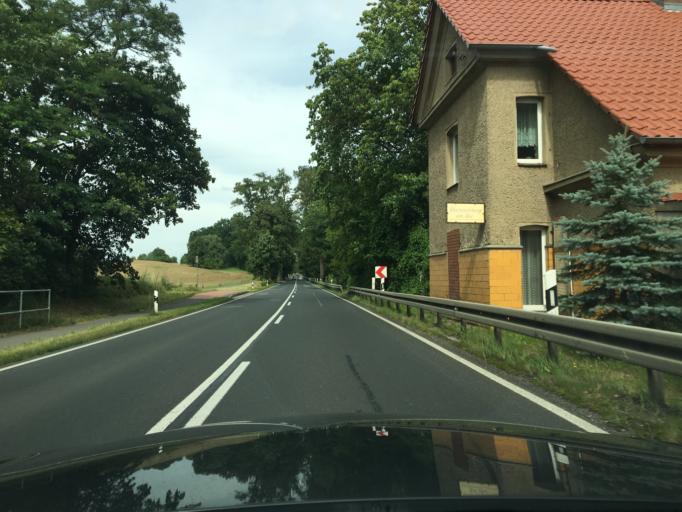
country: DE
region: Mecklenburg-Vorpommern
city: Neustrelitz
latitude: 53.3937
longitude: 13.0993
